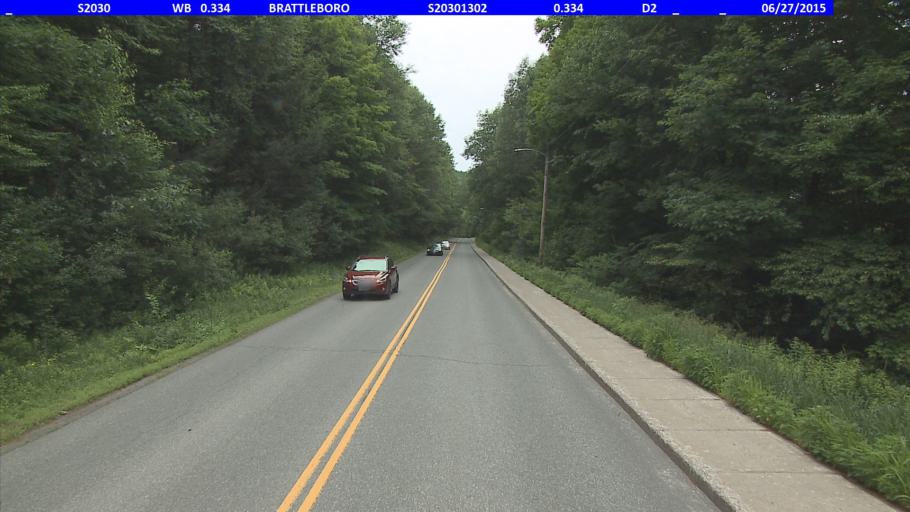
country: US
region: Vermont
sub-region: Windham County
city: Brattleboro
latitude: 42.8461
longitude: -72.5769
